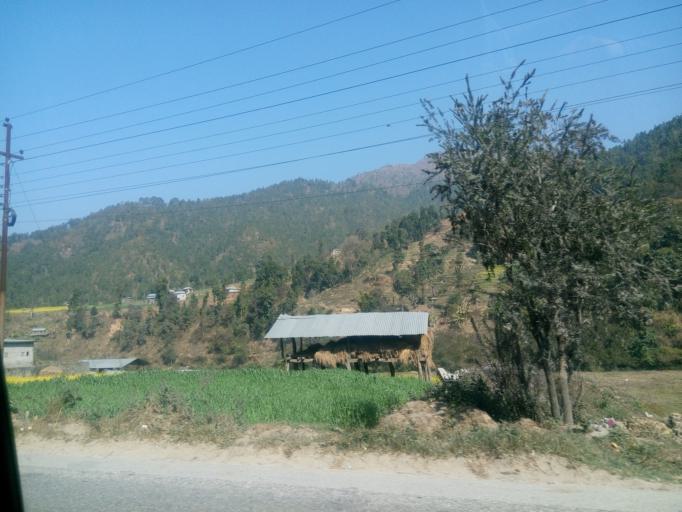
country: NP
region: Central Region
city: Kirtipur
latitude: 27.7663
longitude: 85.0424
